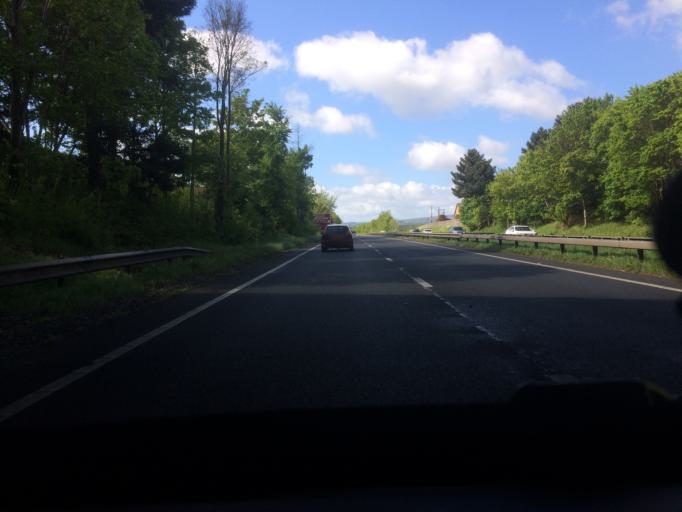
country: GB
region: Wales
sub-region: Wrexham
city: Wrexham
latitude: 53.0648
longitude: -2.9997
